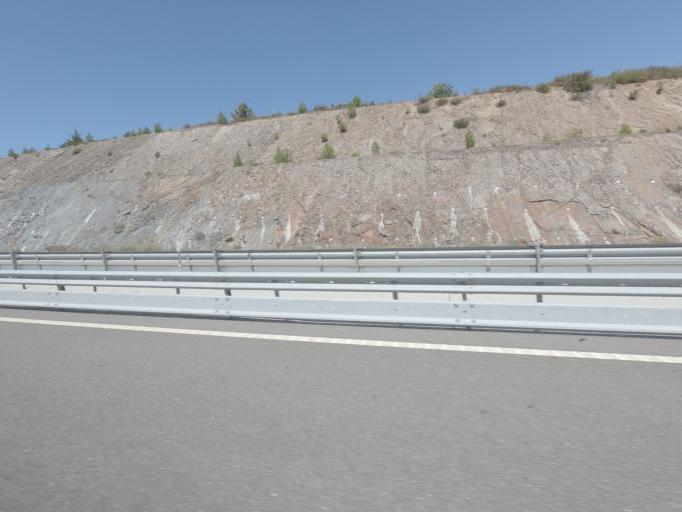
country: PT
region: Vila Real
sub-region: Santa Marta de Penaguiao
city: Santa Marta de Penaguiao
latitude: 41.2684
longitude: -7.8153
